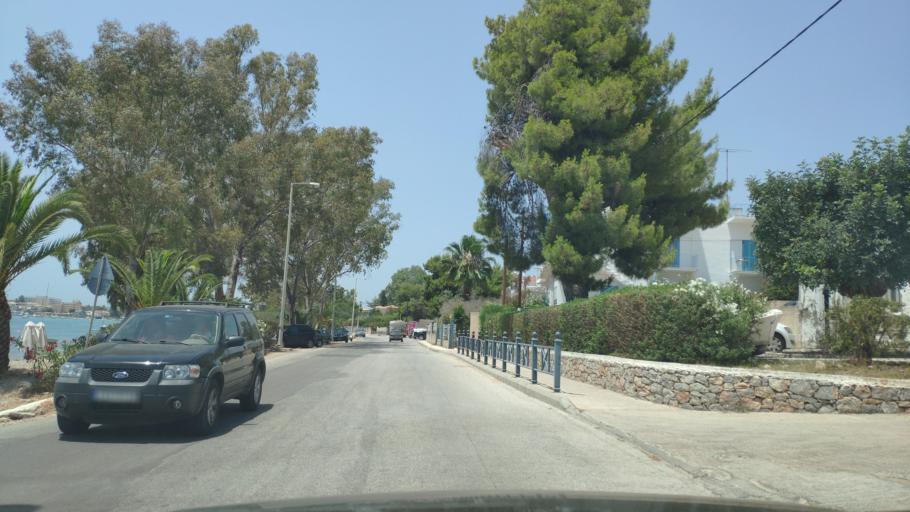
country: GR
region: Peloponnese
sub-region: Nomos Argolidos
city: Porto Cheli
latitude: 37.3238
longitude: 23.1558
